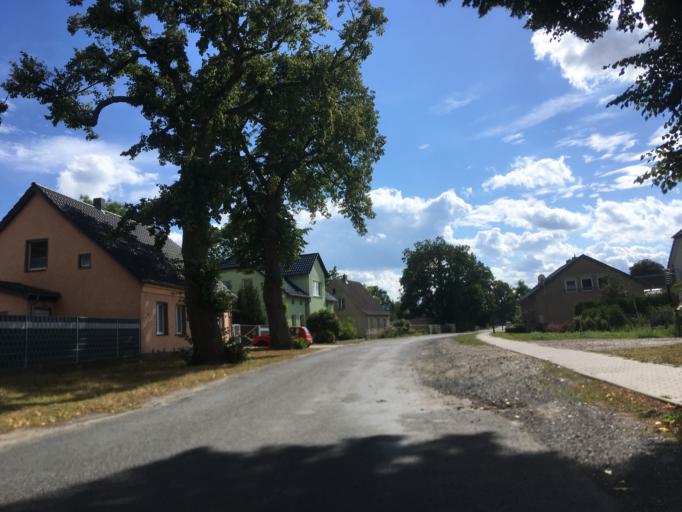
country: DE
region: Brandenburg
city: Angermunde
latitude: 52.9752
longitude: 13.9873
